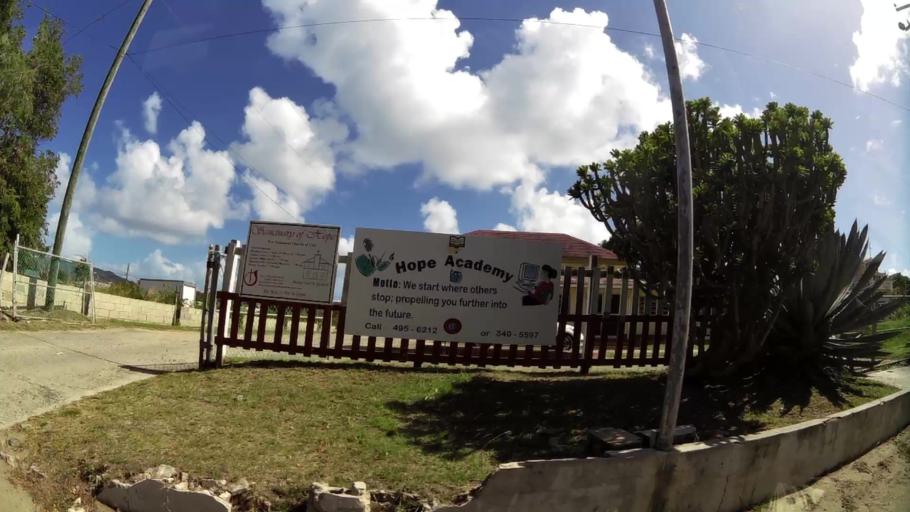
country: VG
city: Tortola
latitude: 18.4417
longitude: -64.4383
